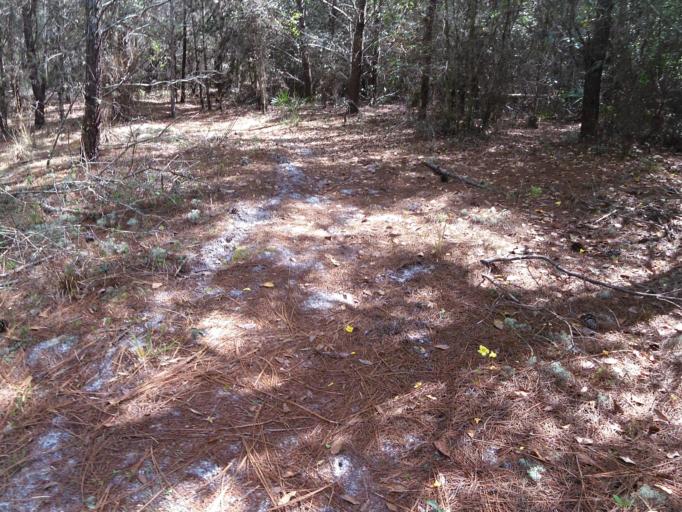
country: US
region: Florida
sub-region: Putnam County
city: Interlachen
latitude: 29.7683
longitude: -81.8664
